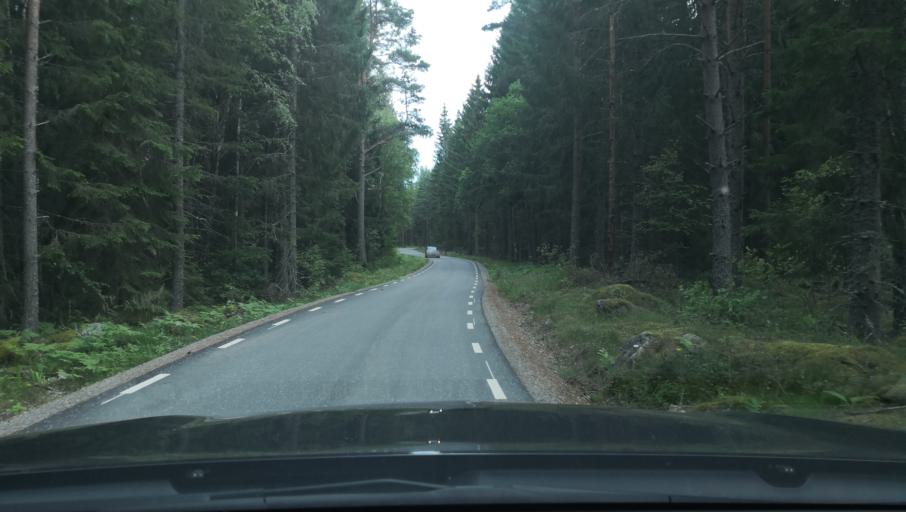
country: SE
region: Vaestmanland
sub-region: Surahammars Kommun
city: Surahammar
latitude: 59.6626
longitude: 16.1321
